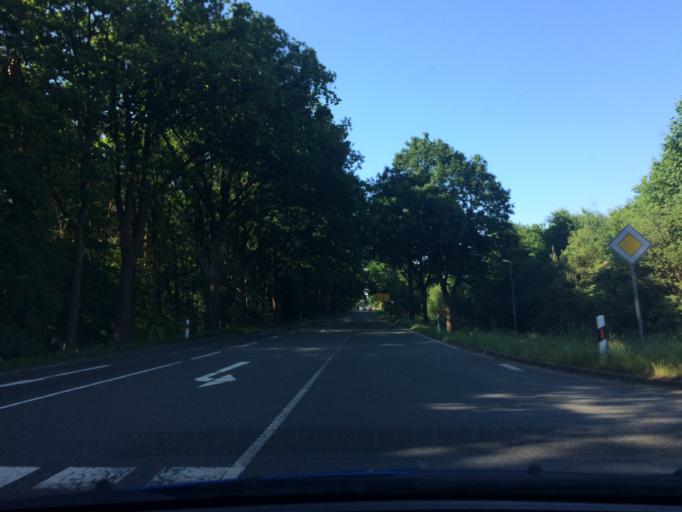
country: DE
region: Lower Saxony
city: Soltau
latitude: 53.0230
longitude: 9.8494
